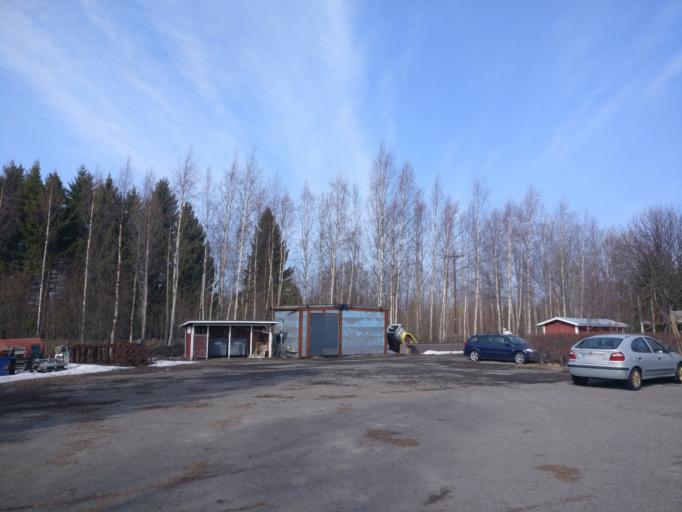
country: FI
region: Lapland
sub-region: Kemi-Tornio
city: Kemi
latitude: 65.7566
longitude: 24.5472
